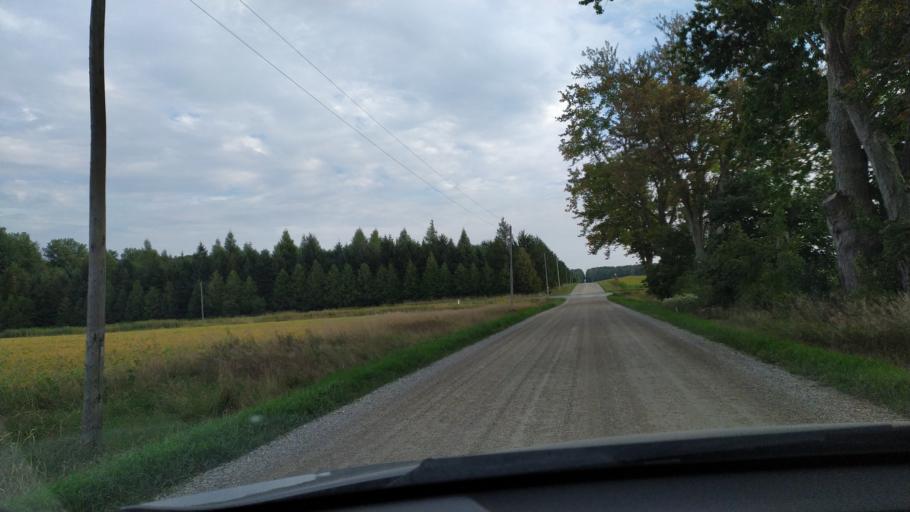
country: CA
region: Ontario
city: Stratford
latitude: 43.4081
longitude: -80.9130
